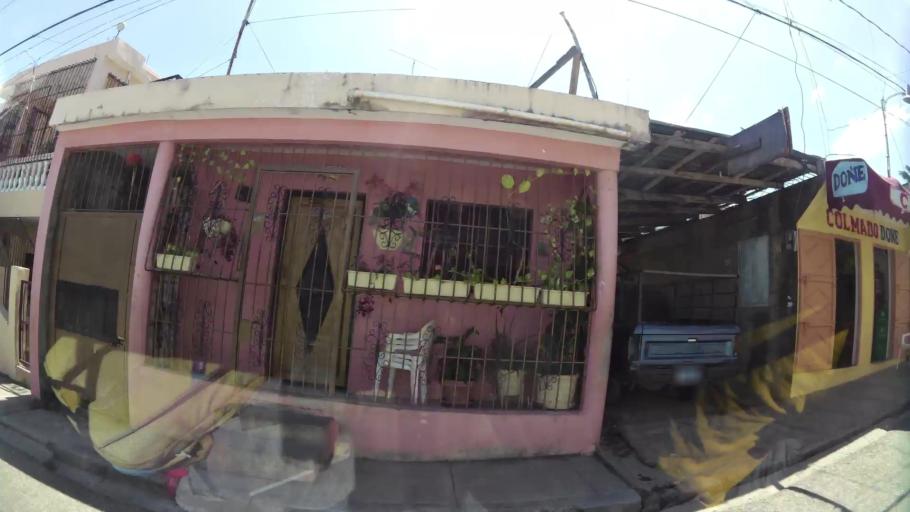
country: DO
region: San Cristobal
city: San Cristobal
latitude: 18.4043
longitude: -70.1113
